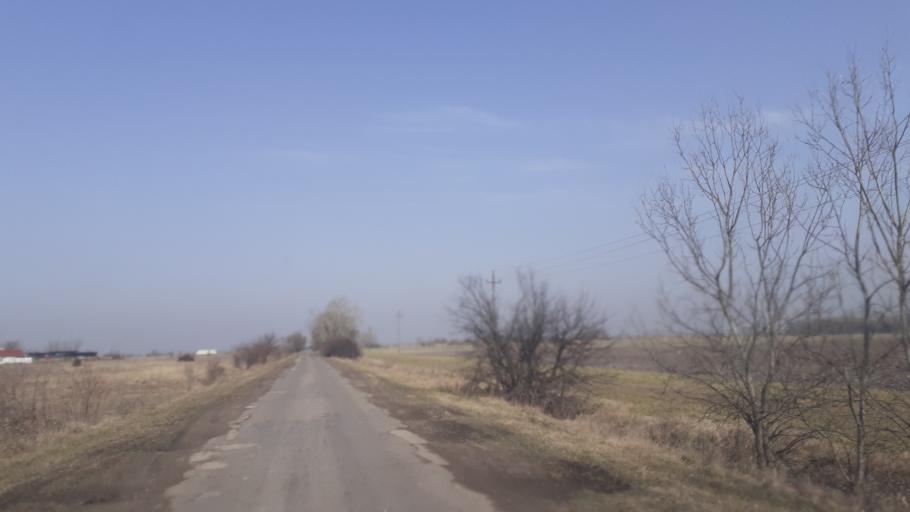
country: HU
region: Pest
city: Dabas
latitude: 47.0677
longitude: 19.2576
